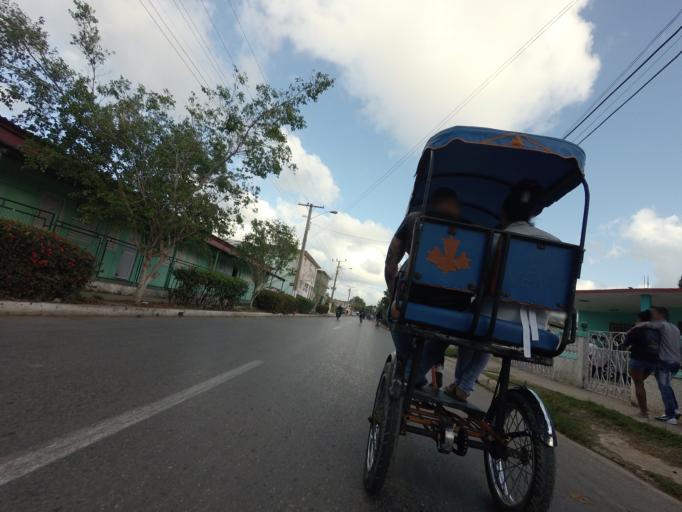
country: CU
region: Ciego de Avila
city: Ciego de Avila
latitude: 21.8407
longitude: -78.7517
